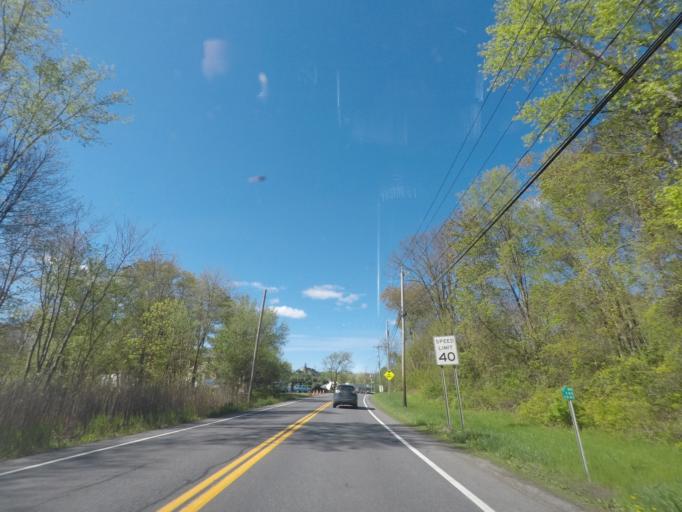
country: US
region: New York
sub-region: Albany County
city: Delmar
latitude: 42.5872
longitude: -73.7972
